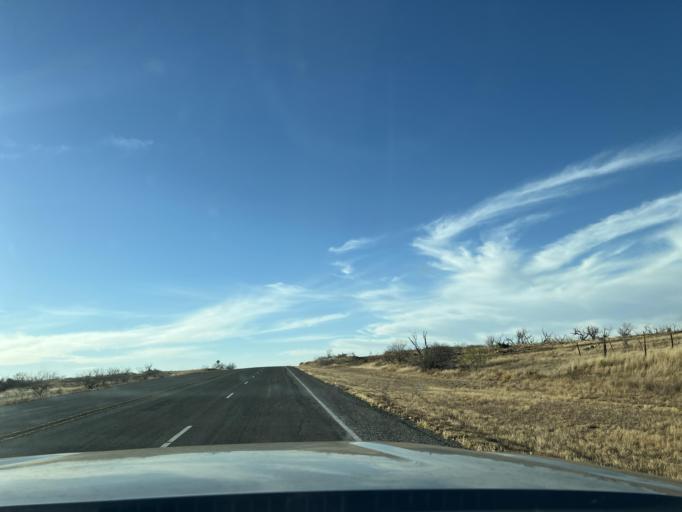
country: US
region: Texas
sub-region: Borden County
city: Gail
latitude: 32.7599
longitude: -101.2614
